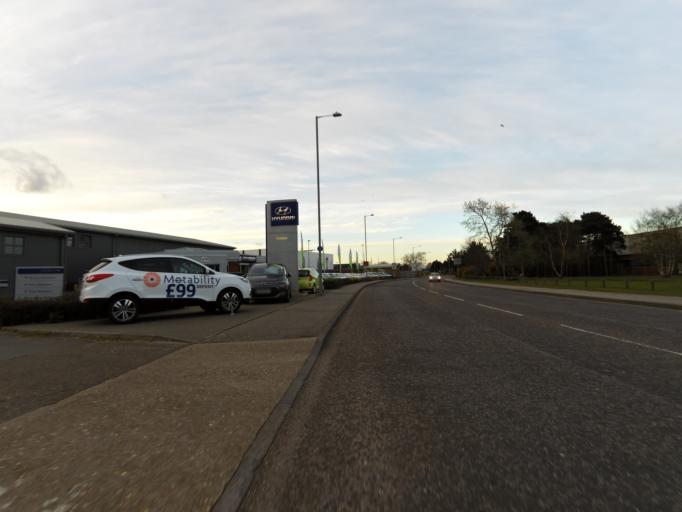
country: GB
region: England
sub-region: Suffolk
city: Kesgrave
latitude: 52.0313
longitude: 1.2025
